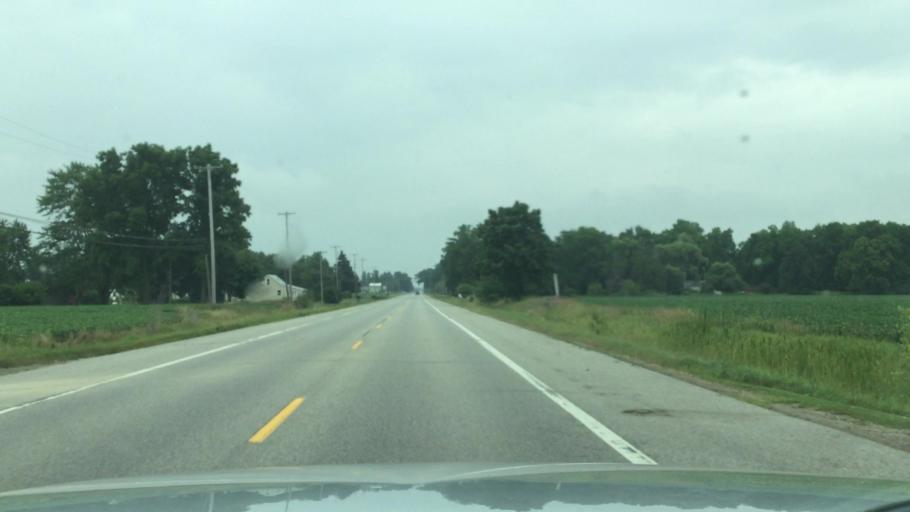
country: US
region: Michigan
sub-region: Shiawassee County
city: New Haven
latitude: 43.0489
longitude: -84.1771
